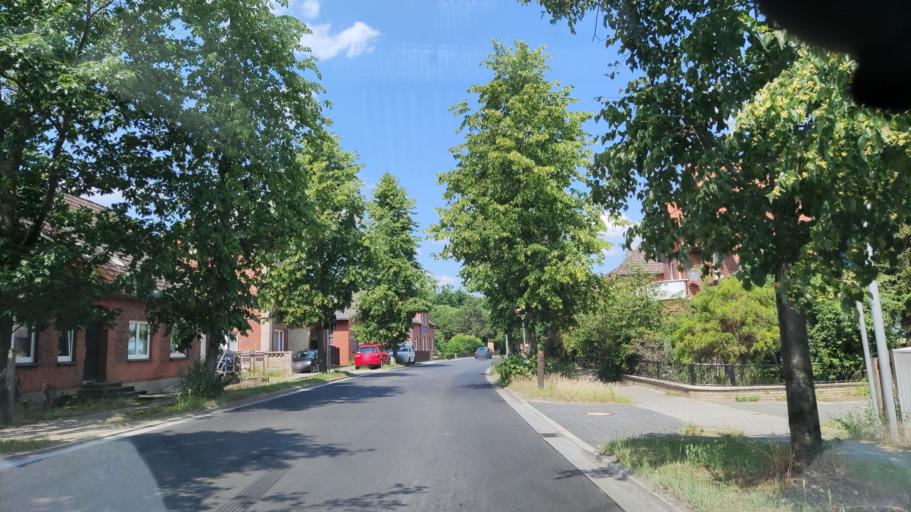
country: DE
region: Lower Saxony
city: Gerdau
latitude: 52.9632
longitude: 10.4170
